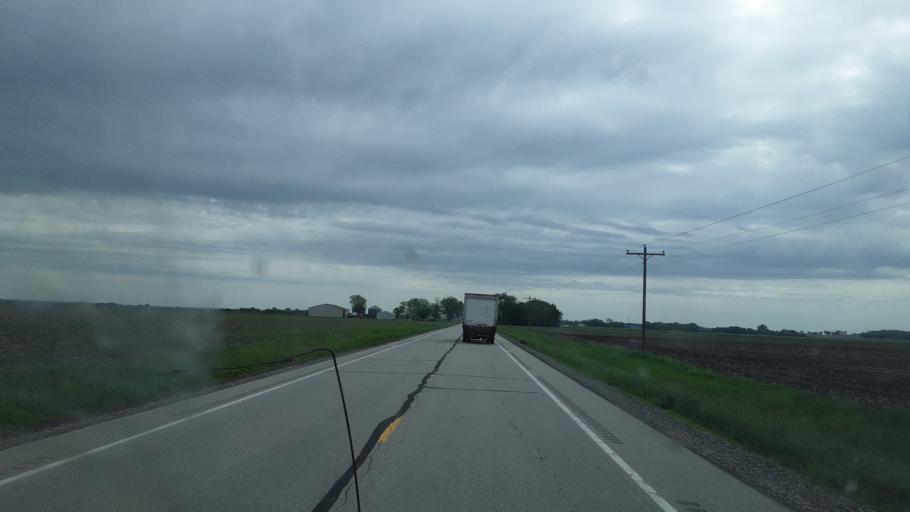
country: US
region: Illinois
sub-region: Mason County
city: Mason City
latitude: 40.3047
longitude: -89.7040
